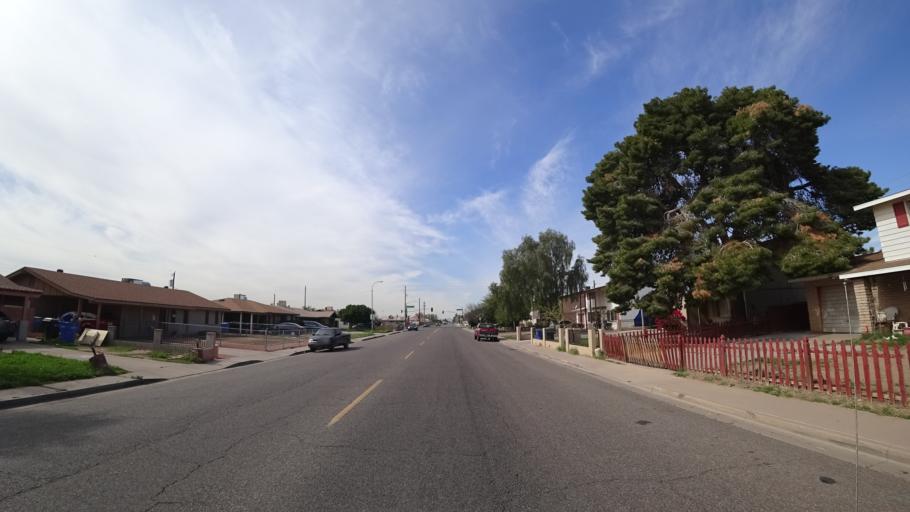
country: US
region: Arizona
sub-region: Maricopa County
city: Tolleson
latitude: 33.4871
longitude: -112.2363
